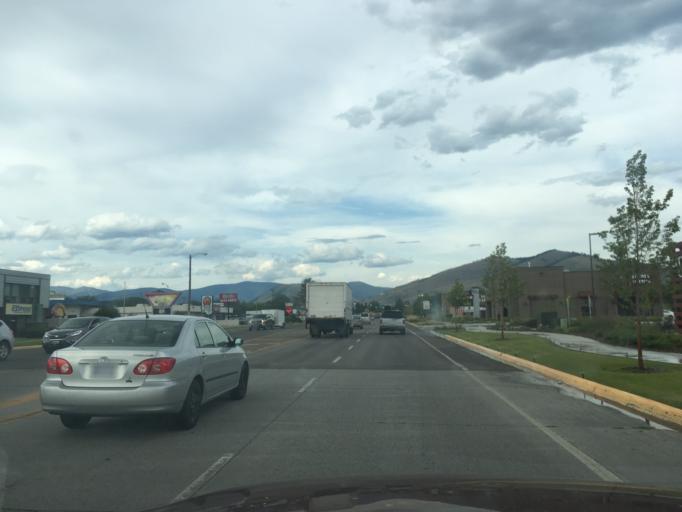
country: US
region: Montana
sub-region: Missoula County
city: Orchard Homes
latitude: 46.8367
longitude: -114.0389
